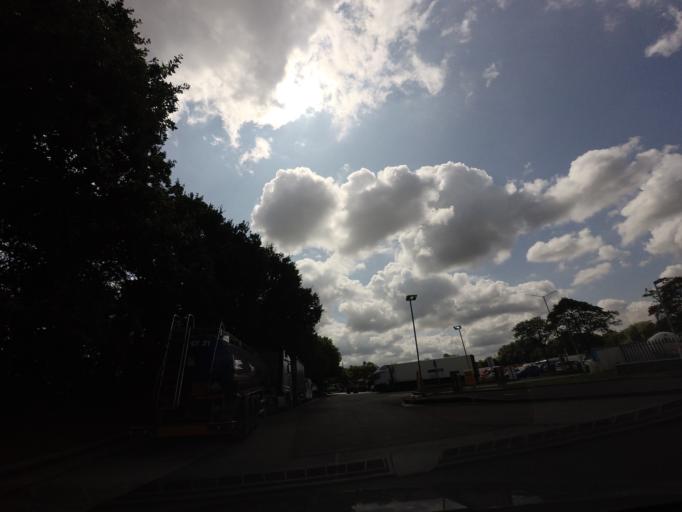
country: GB
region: England
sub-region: Lancashire
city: Coppull
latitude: 53.6321
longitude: -2.6891
